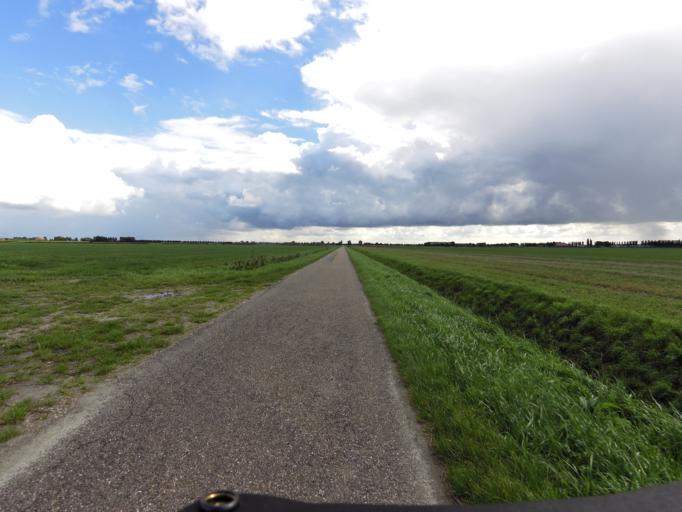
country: NL
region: North Brabant
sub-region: Gemeente Steenbergen
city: Nieuw-Vossemeer
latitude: 51.6828
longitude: 4.2350
